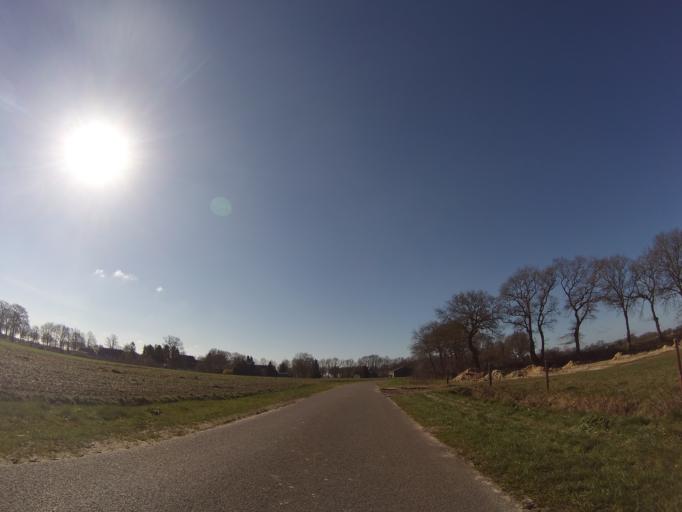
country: NL
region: Drenthe
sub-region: Gemeente Coevorden
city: Sleen
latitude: 52.7608
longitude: 6.8283
